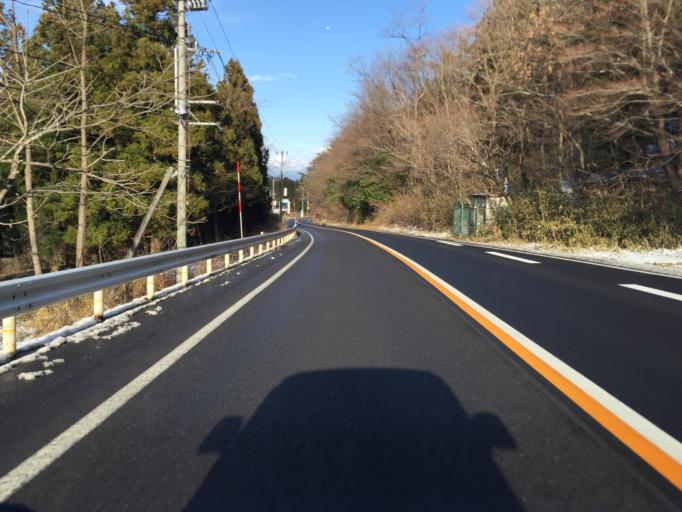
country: JP
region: Fukushima
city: Fukushima-shi
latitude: 37.6973
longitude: 140.3485
